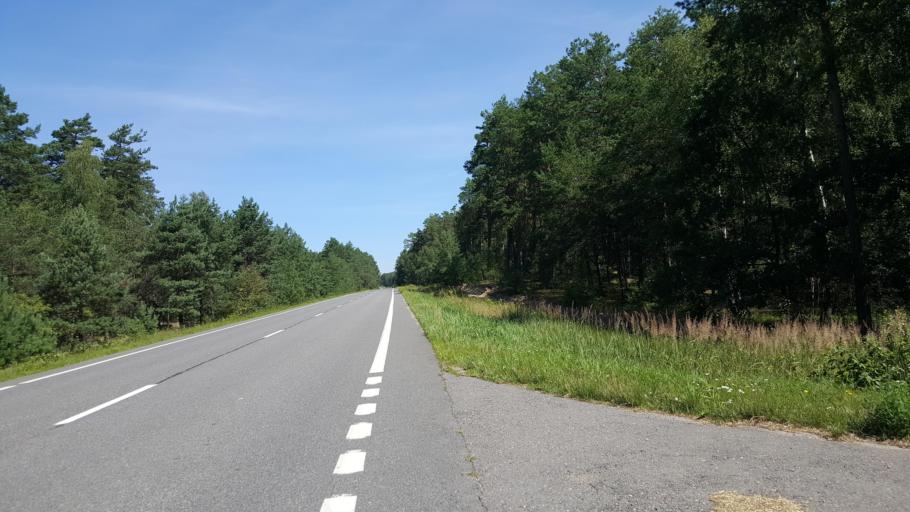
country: BY
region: Brest
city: Zhabinka
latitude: 52.4215
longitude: 24.1210
